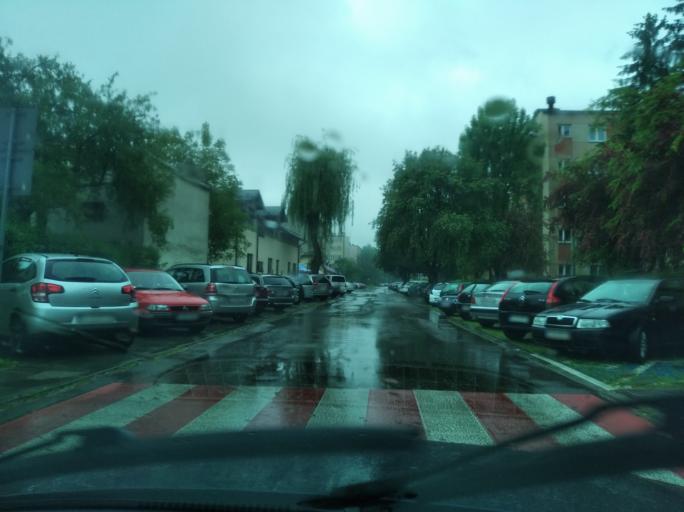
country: PL
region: Subcarpathian Voivodeship
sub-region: Powiat jasielski
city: Jaslo
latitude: 49.7380
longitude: 21.4640
